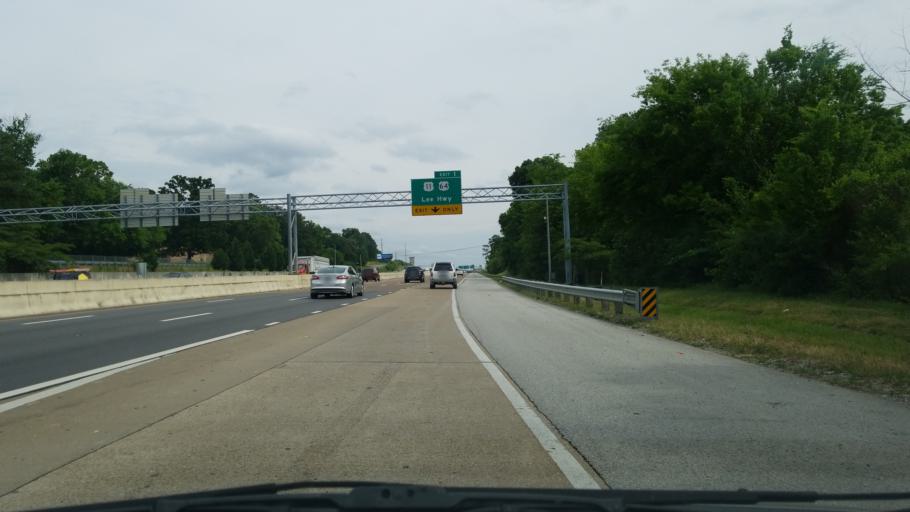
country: US
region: Tennessee
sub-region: Hamilton County
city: East Brainerd
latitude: 35.0407
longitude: -85.1859
